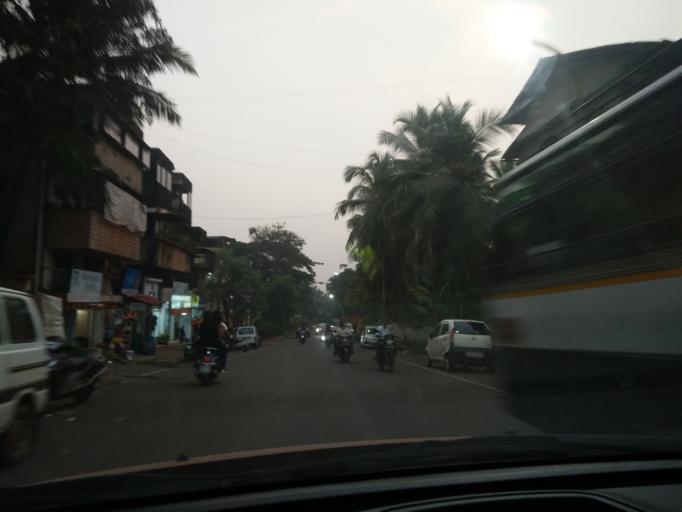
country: IN
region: Goa
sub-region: South Goa
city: Madgaon
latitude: 15.2749
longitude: 73.9736
